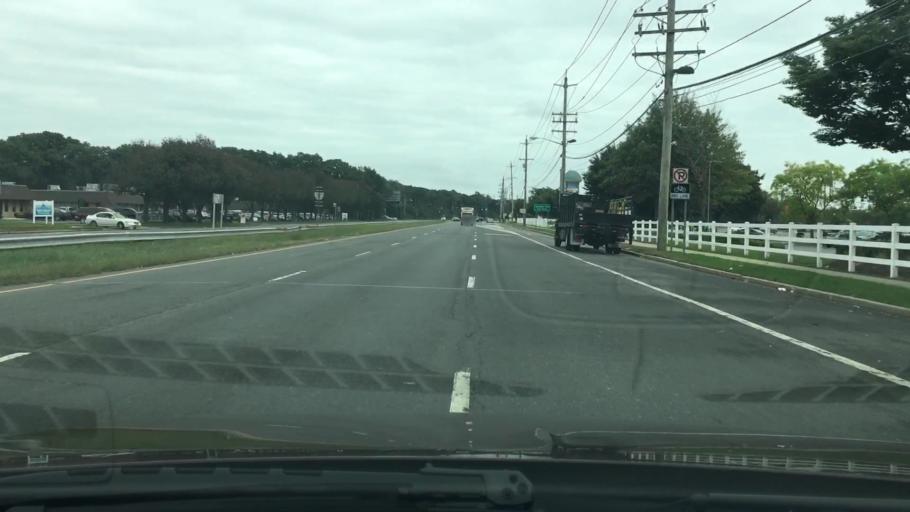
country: US
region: New York
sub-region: Suffolk County
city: Islandia
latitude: 40.8054
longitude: -73.1806
